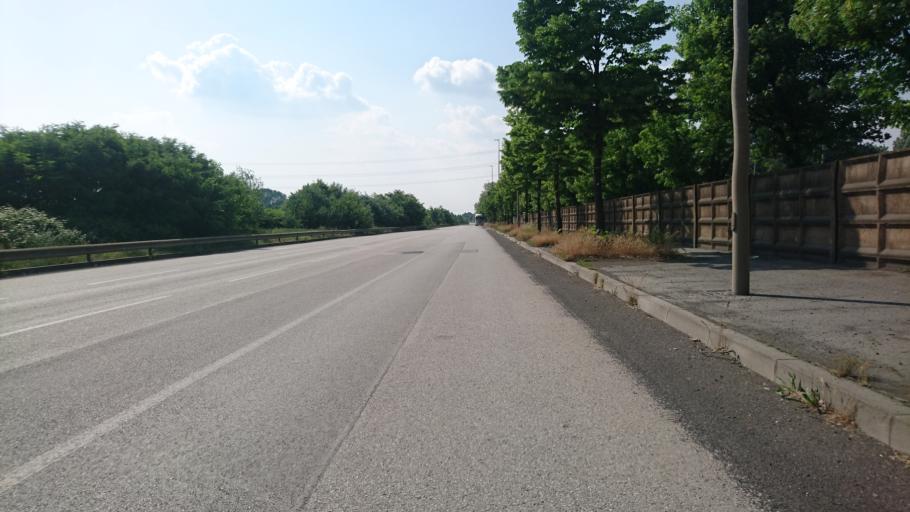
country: IT
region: Veneto
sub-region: Provincia di Padova
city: Villatora
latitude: 45.3799
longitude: 11.9491
